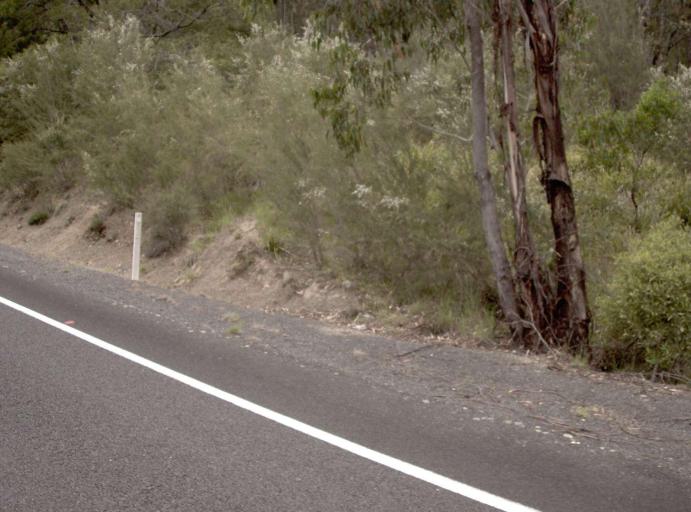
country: AU
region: New South Wales
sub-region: Bombala
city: Bombala
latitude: -37.2456
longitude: 149.2589
